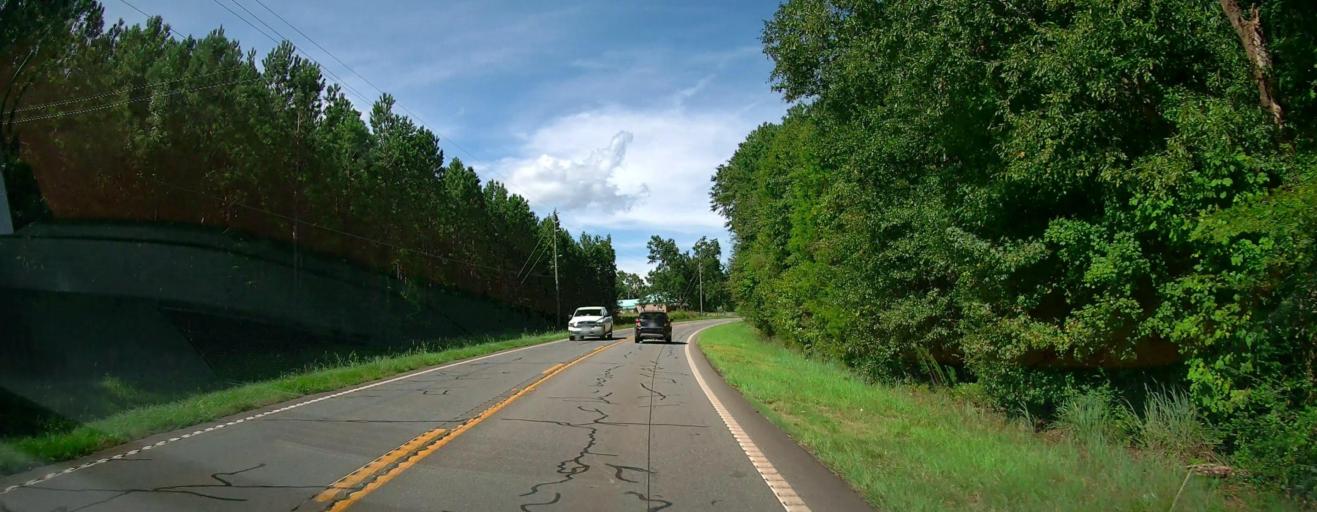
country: US
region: Georgia
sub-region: Talbot County
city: Sardis
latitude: 32.7664
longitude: -84.5586
